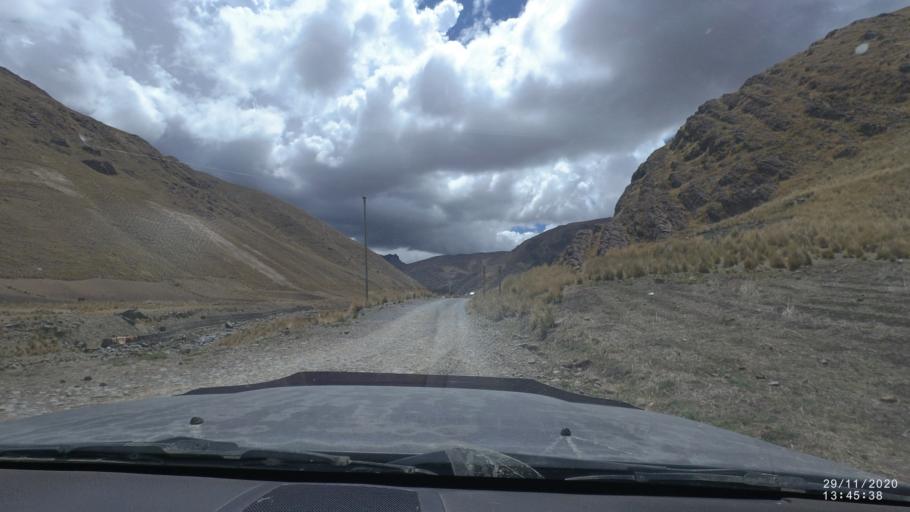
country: BO
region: Cochabamba
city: Cochabamba
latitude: -17.1491
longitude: -66.3216
